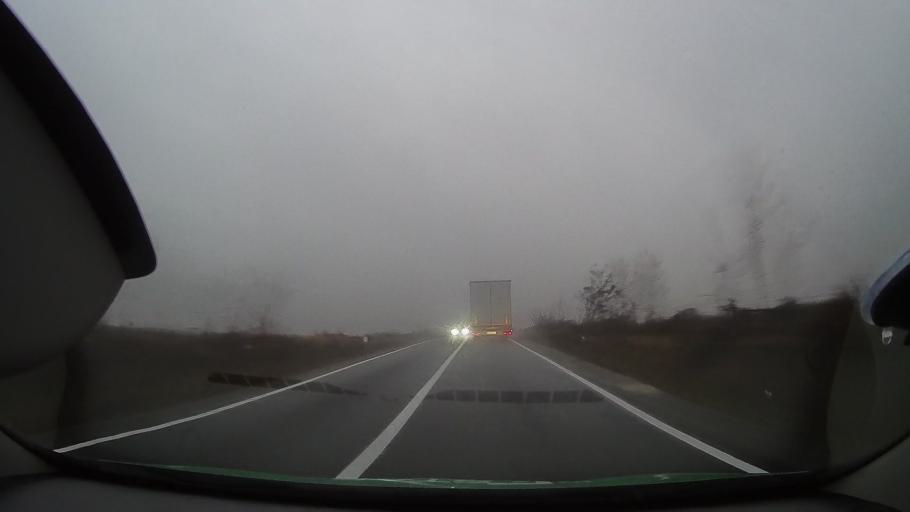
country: RO
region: Bihor
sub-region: Comuna Olcea
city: Calacea
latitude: 46.6564
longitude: 21.9606
